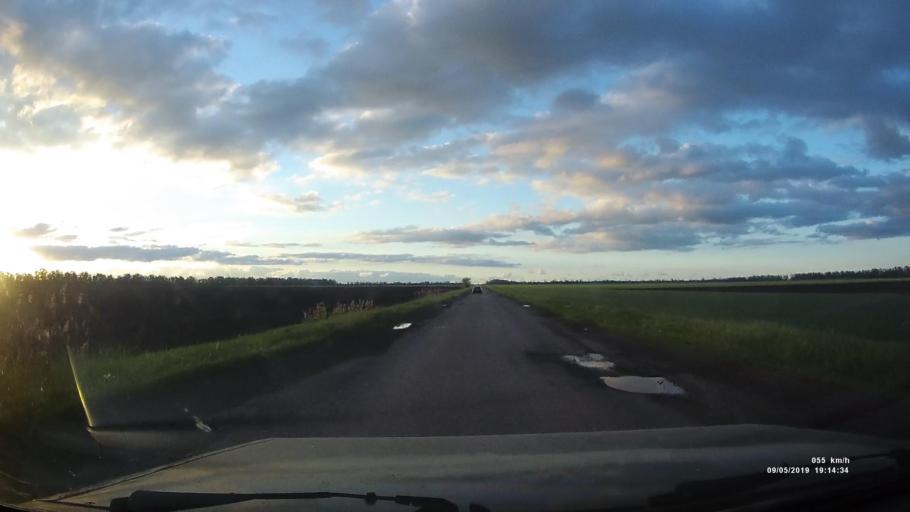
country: RU
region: Krasnodarskiy
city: Kanelovskaya
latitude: 46.7599
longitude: 39.2143
